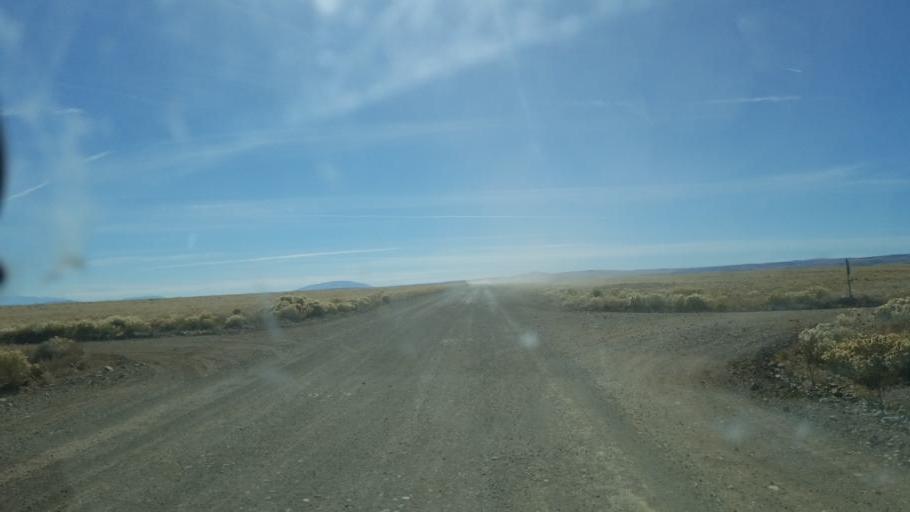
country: US
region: Colorado
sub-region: Rio Grande County
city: Monte Vista
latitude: 37.3433
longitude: -106.1490
